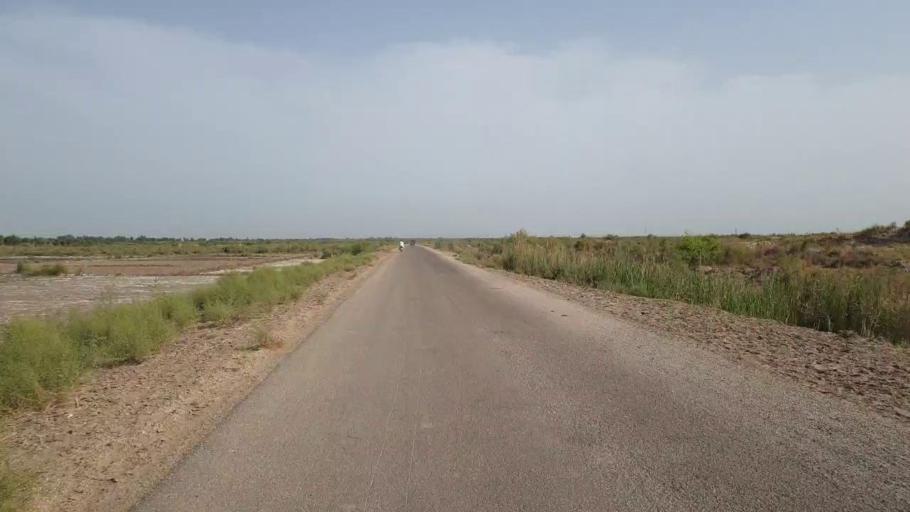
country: PK
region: Sindh
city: Sakrand
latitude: 26.2766
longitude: 68.2714
